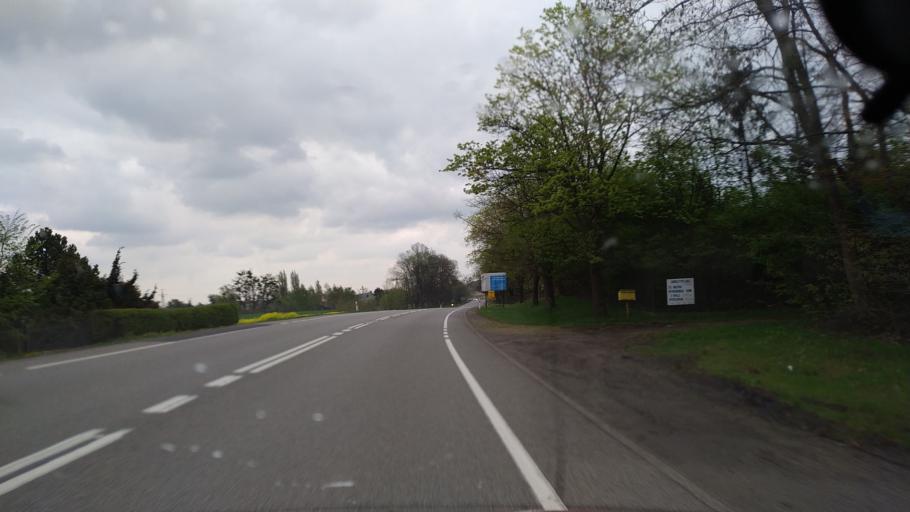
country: PL
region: Pomeranian Voivodeship
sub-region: Powiat tczewski
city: Subkowy
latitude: 54.0485
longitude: 18.7499
